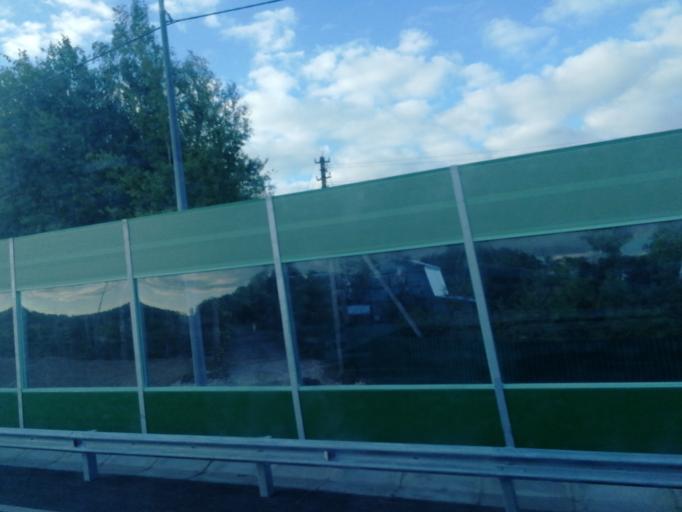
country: RU
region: Kaluga
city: Kaluga
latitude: 54.4581
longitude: 36.2776
